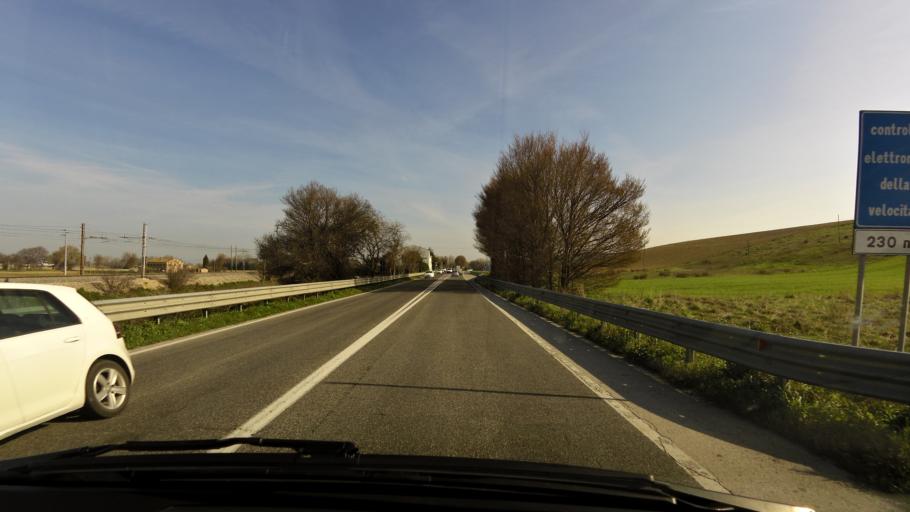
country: IT
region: The Marches
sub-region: Provincia di Ancona
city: Villa Musone
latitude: 43.4678
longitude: 13.6008
